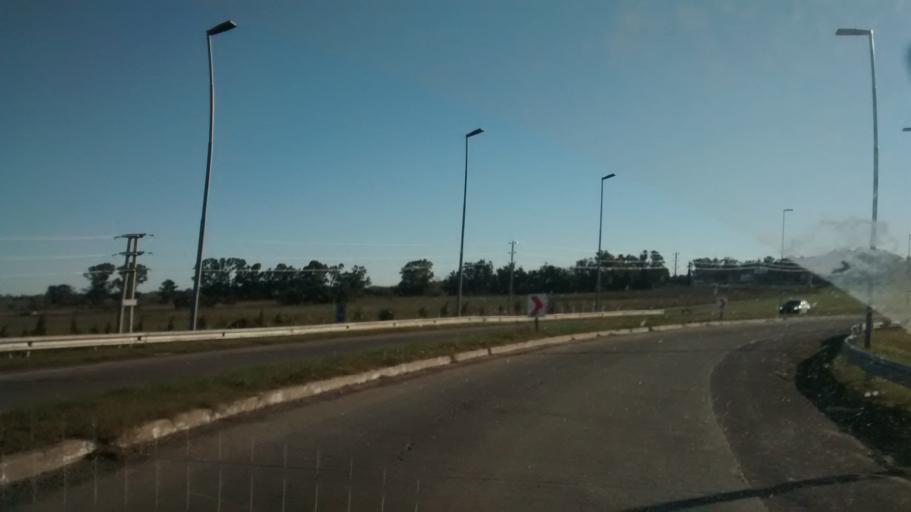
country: AR
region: Buenos Aires
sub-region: Partido de La Plata
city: La Plata
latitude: -35.0357
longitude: -58.0940
